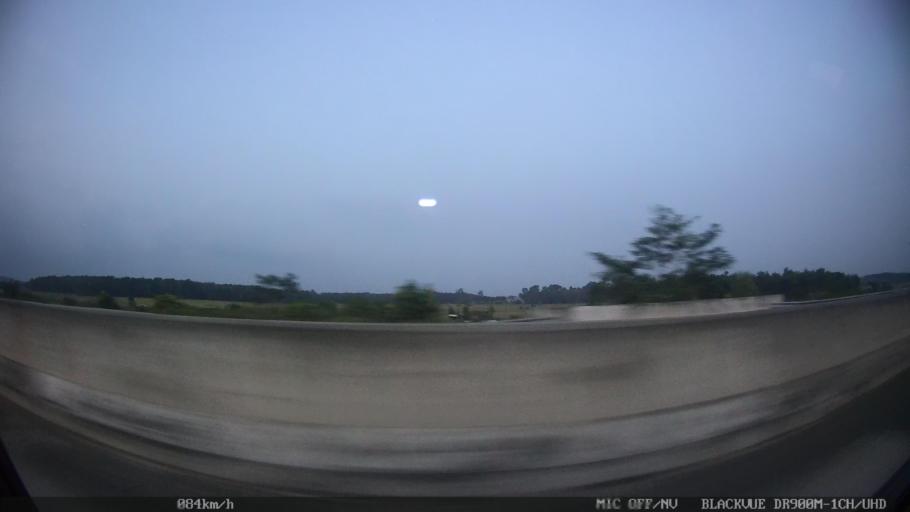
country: ID
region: Lampung
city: Sidorejo
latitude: -5.5851
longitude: 105.5445
